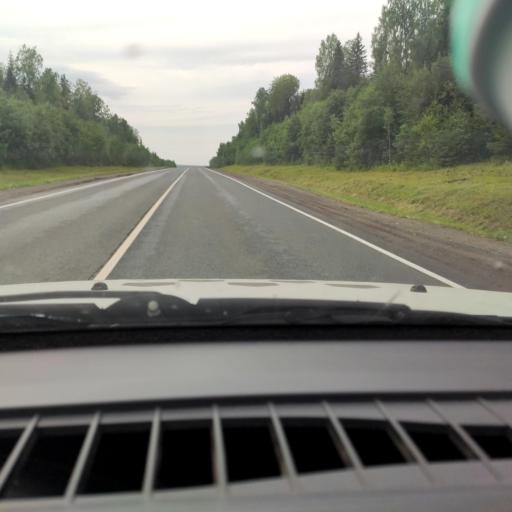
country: RU
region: Kirov
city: Kostino
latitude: 58.7876
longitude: 53.6026
